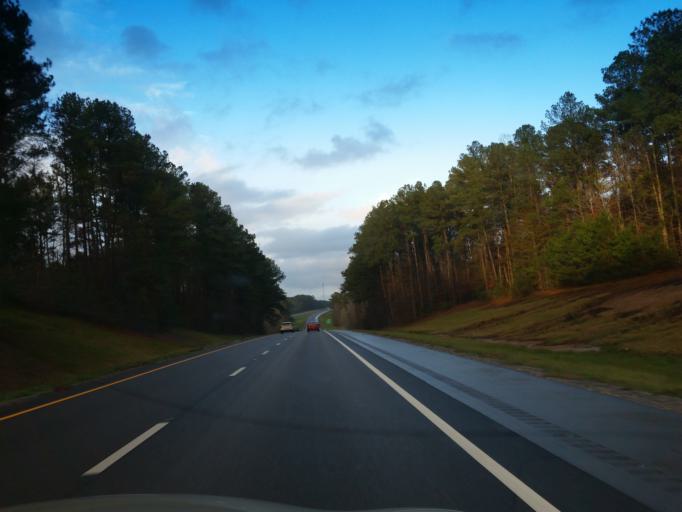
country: US
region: Mississippi
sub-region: Jones County
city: Sharon
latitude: 31.9527
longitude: -88.9786
